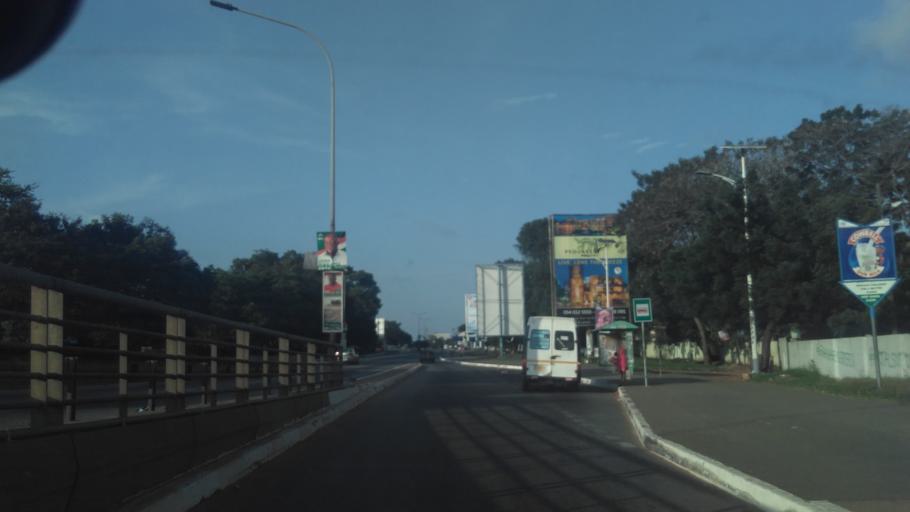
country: GH
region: Greater Accra
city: Accra
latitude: 5.5731
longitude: -0.1897
